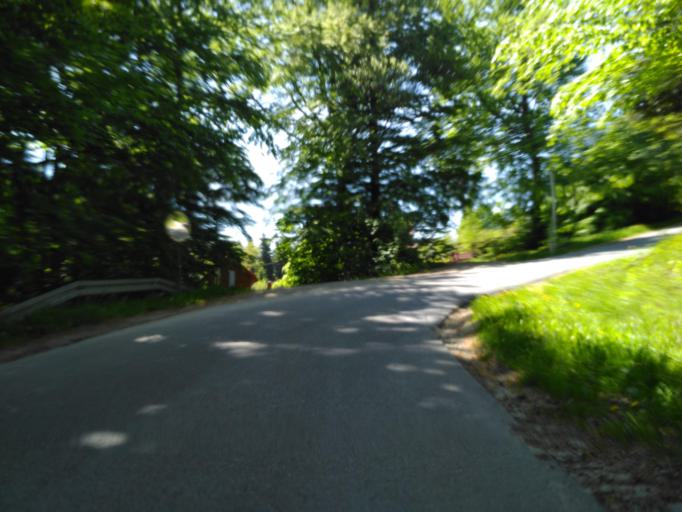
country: PL
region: Subcarpathian Voivodeship
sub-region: Powiat krosnienski
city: Iwonicz-Zdroj
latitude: 49.5517
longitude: 21.7795
